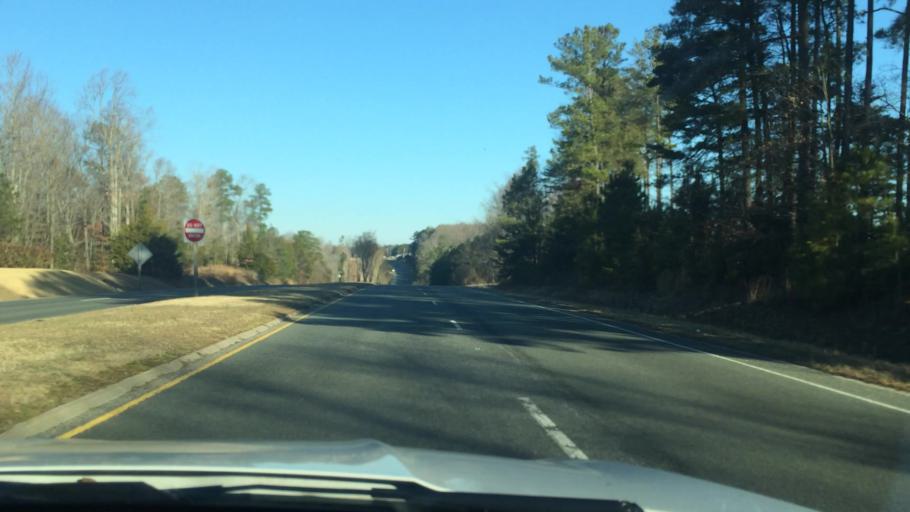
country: US
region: Virginia
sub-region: Lancaster County
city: Kilmarnock
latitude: 37.7288
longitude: -76.3902
